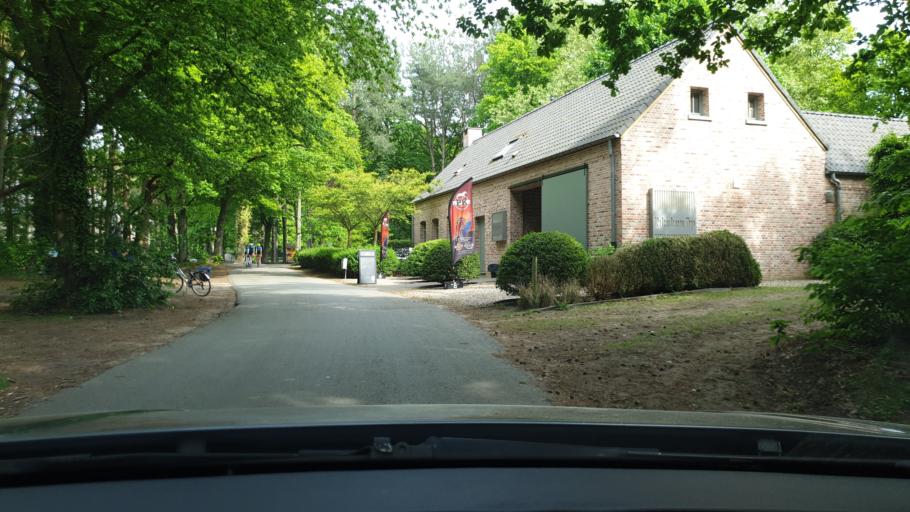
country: BE
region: Flanders
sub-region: Provincie Antwerpen
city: Laakdal
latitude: 51.0544
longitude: 5.0375
